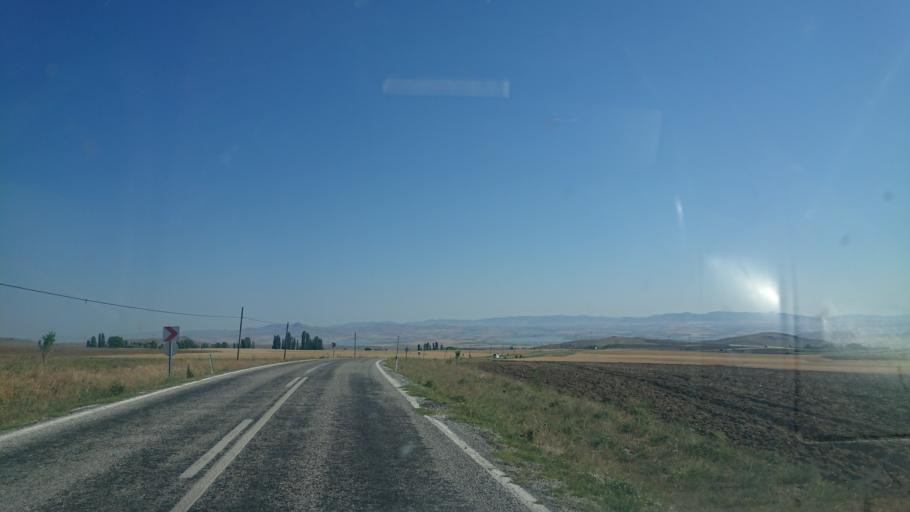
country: TR
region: Aksaray
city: Sariyahsi
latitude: 38.9363
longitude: 33.8328
